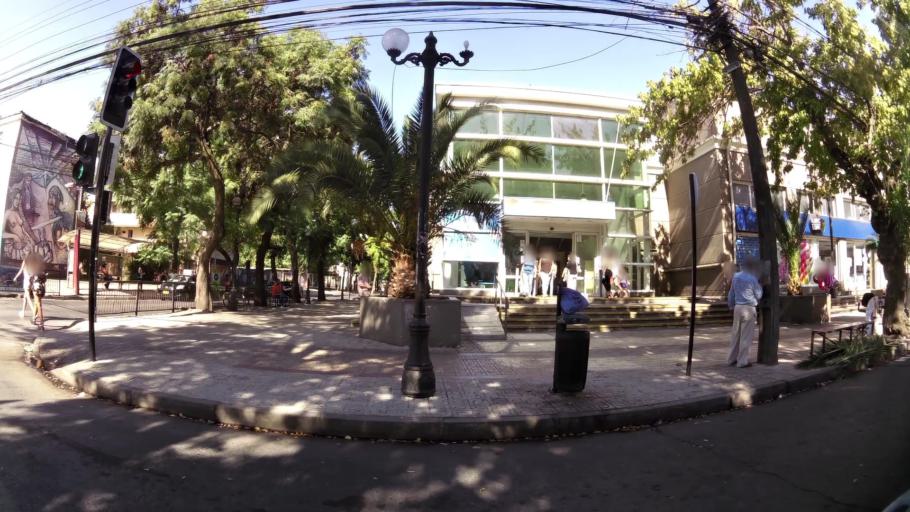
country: CL
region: Maule
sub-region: Provincia de Talca
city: Talca
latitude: -35.4256
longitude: -71.6554
